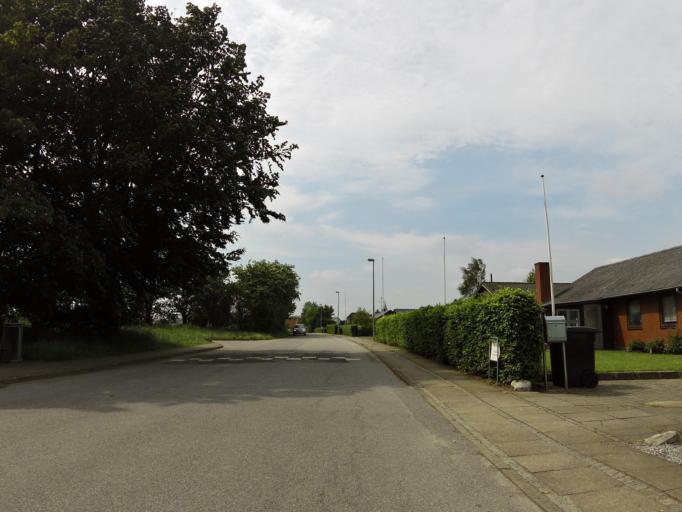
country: DK
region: South Denmark
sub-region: Haderslev Kommune
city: Gram
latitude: 55.2728
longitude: 9.1773
